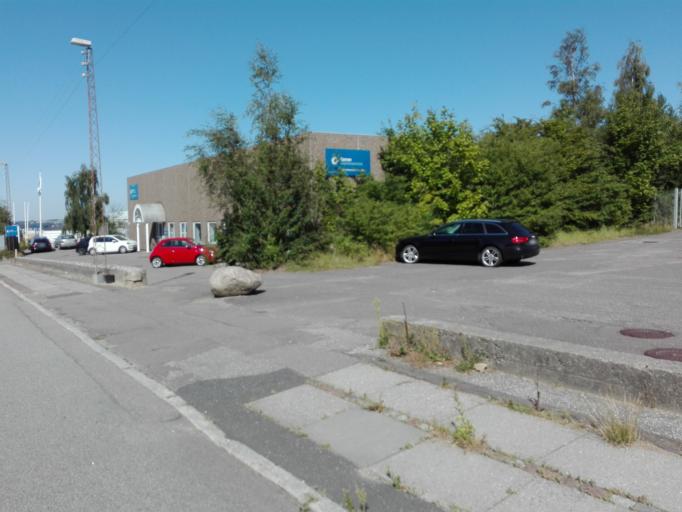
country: DK
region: Central Jutland
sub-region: Arhus Kommune
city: Tranbjerg
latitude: 56.1083
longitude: 10.1332
